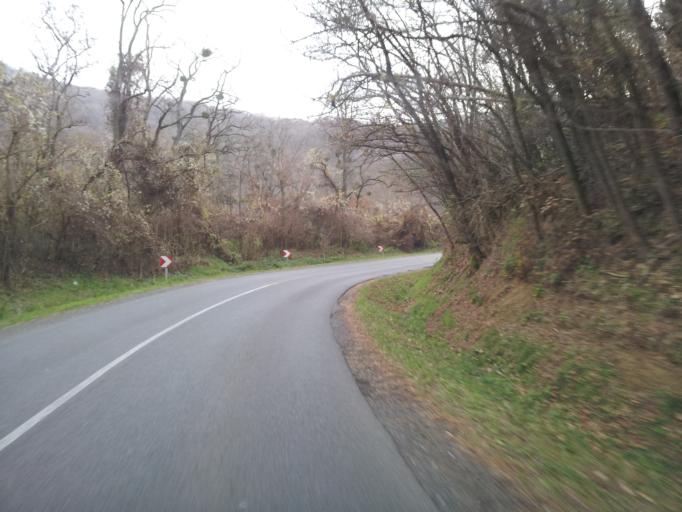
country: HU
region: Zala
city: Cserszegtomaj
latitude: 46.8727
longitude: 17.2203
